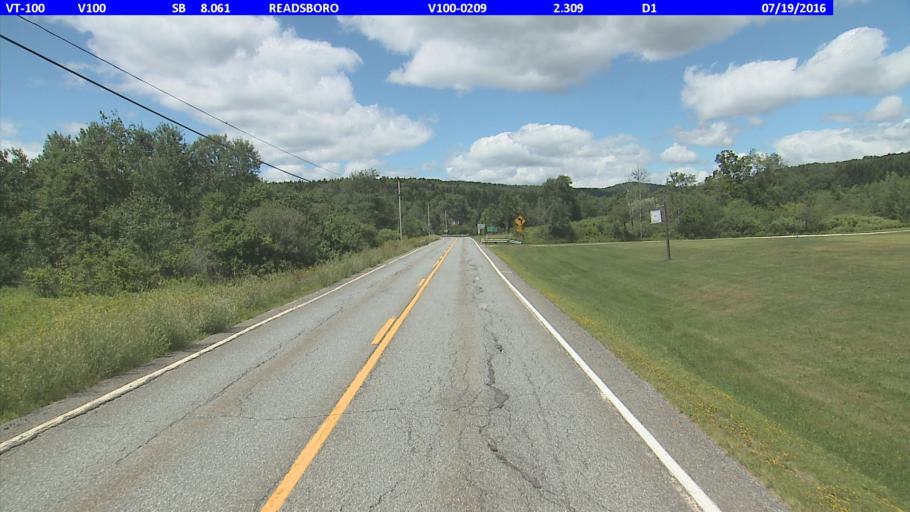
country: US
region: Massachusetts
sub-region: Berkshire County
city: North Adams
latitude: 42.8274
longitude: -72.9863
